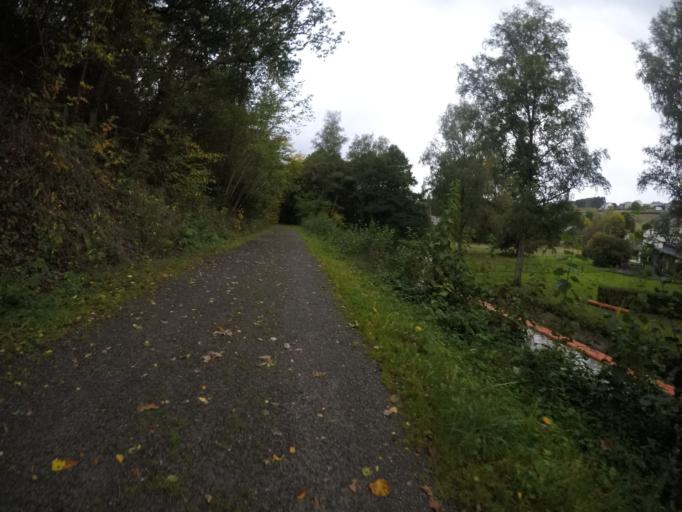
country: BE
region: Wallonia
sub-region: Province du Luxembourg
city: Fauvillers
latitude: 49.8521
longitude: 5.6987
